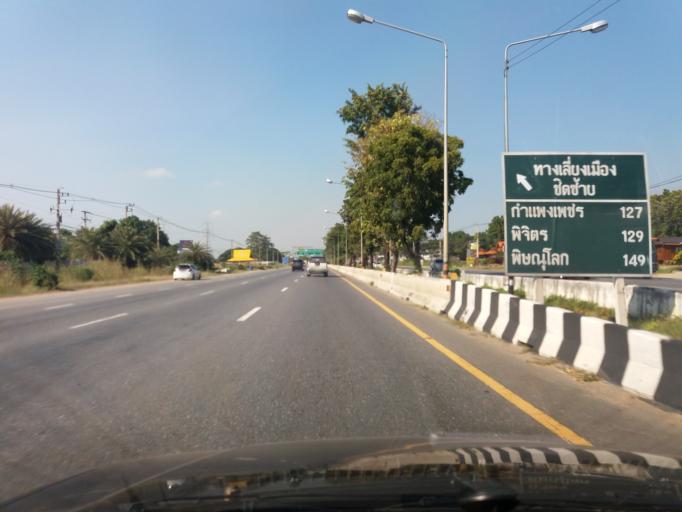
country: TH
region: Nakhon Sawan
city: Krok Phra
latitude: 15.6038
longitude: 100.1221
